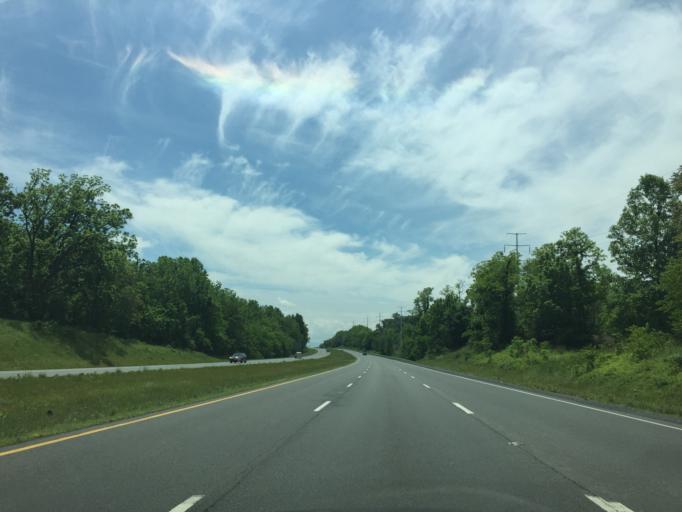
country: US
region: Virginia
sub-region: City of Winchester
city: Winchester
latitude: 39.1559
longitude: -78.2115
